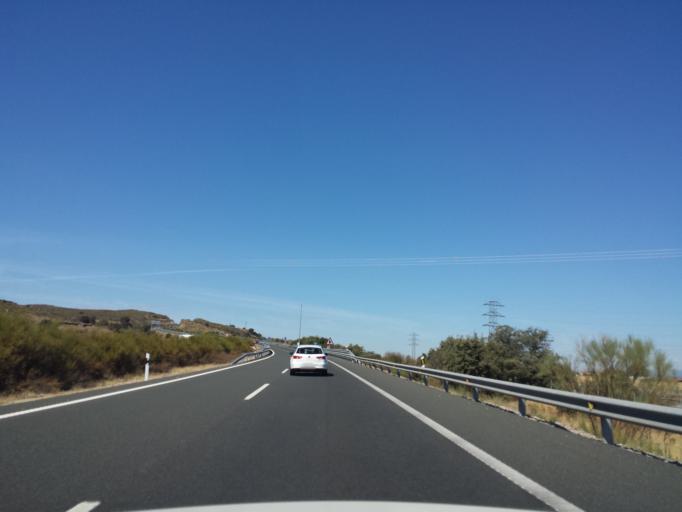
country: ES
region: Extremadura
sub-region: Provincia de Caceres
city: Navalmoral de la Mata
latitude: 39.8903
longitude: -5.5105
